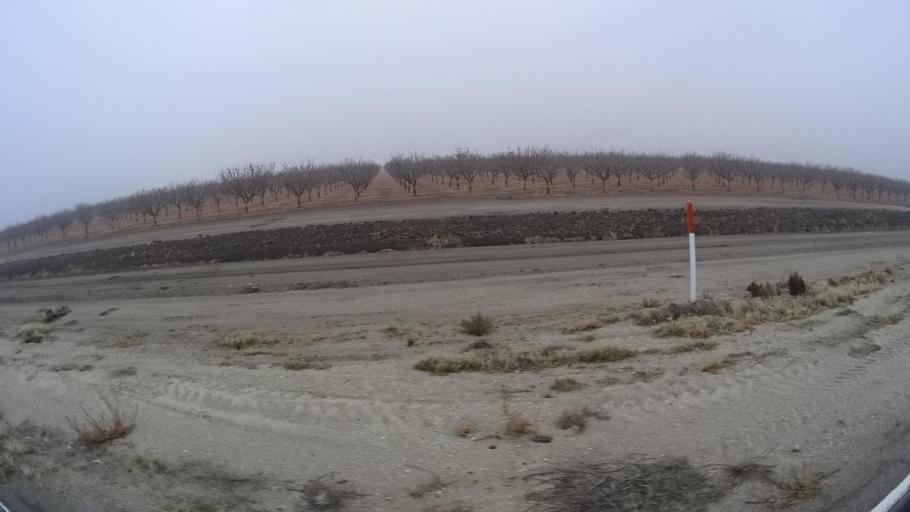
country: US
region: California
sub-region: Kern County
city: Buttonwillow
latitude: 35.4205
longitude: -119.5215
